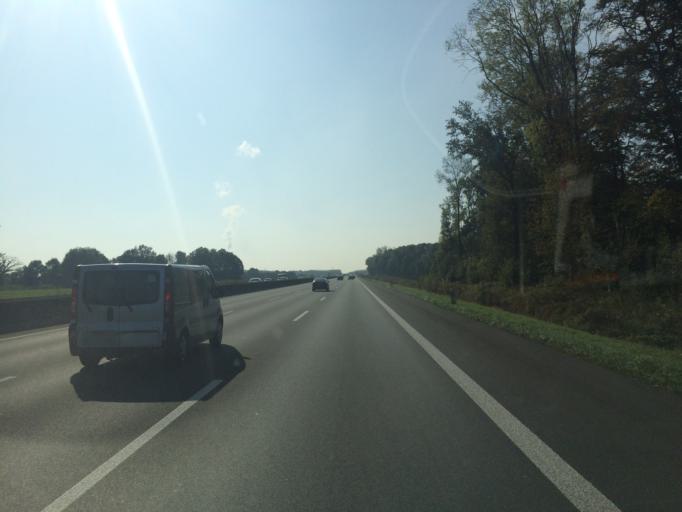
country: DE
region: North Rhine-Westphalia
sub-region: Regierungsbezirk Munster
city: Beckum
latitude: 51.7442
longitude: 7.9920
